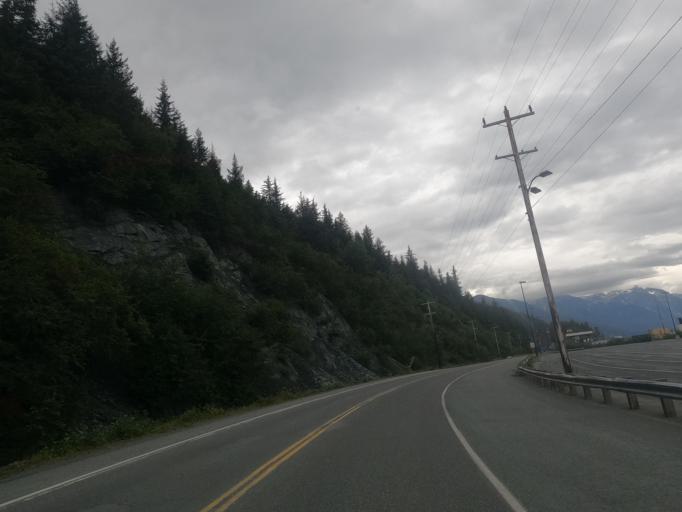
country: US
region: Alaska
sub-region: Haines Borough
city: Haines
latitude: 59.2810
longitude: -135.4635
